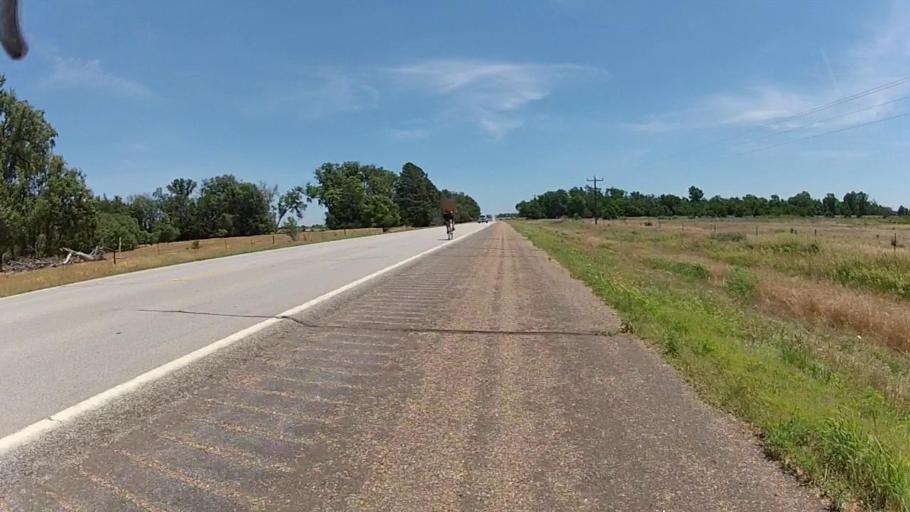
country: US
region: Kansas
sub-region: Barber County
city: Medicine Lodge
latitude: 37.2533
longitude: -98.3274
